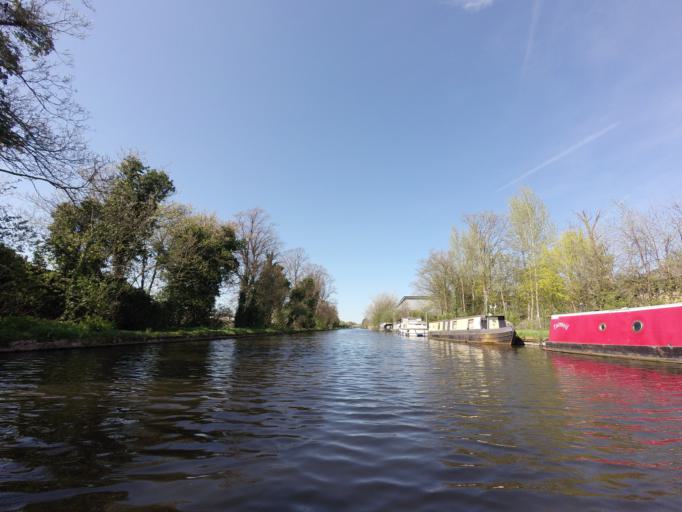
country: GB
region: England
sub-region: Greater London
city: Uxbridge
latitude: 51.5346
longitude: -0.4875
